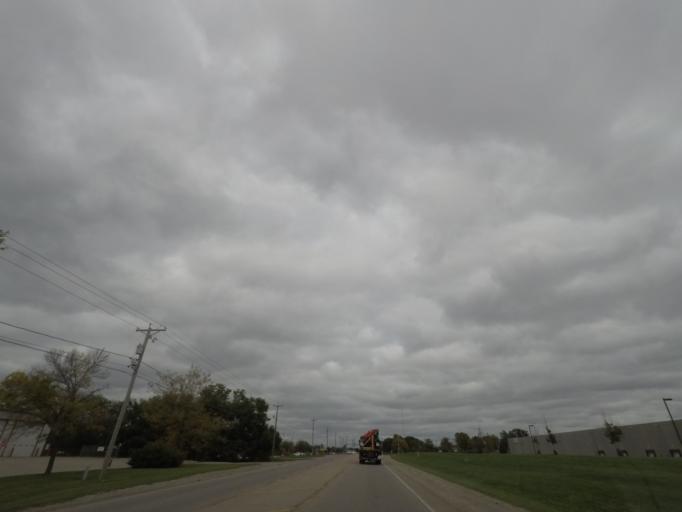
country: US
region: Iowa
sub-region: Polk County
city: Saylorville
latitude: 41.6635
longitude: -93.6005
